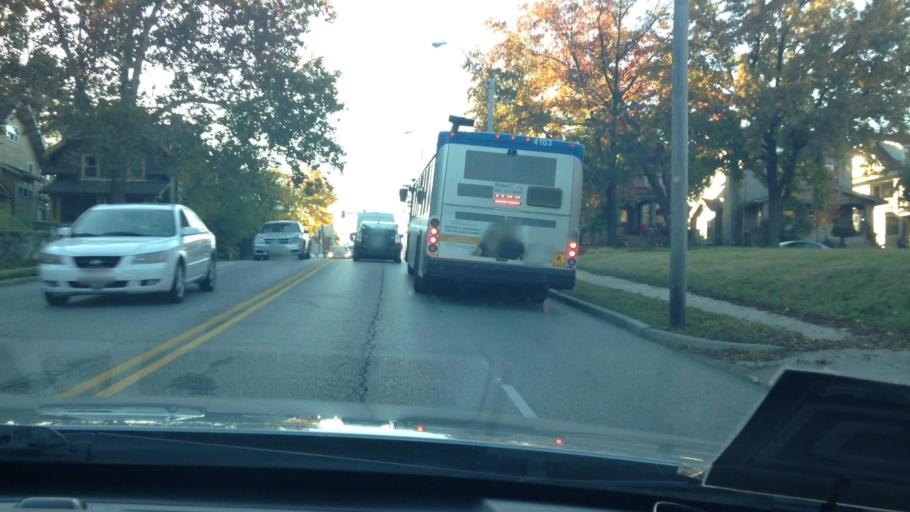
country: US
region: Missouri
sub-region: Jackson County
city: Kansas City
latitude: 39.0561
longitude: -94.5703
